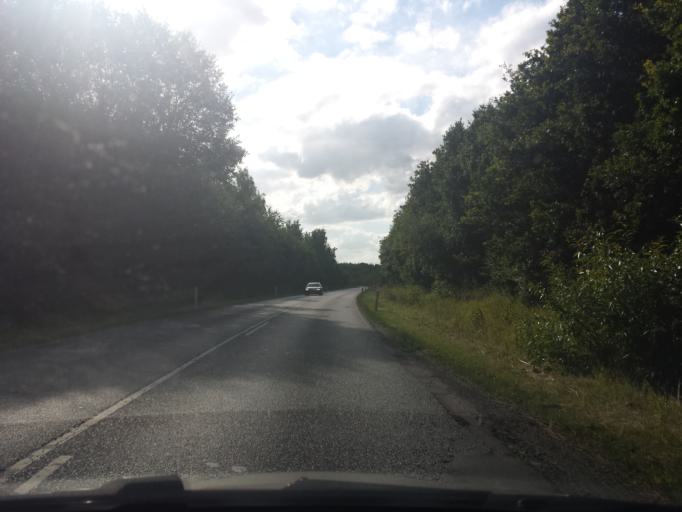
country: DK
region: Capital Region
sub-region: Albertslund Kommune
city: Albertslund
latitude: 55.6824
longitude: 12.3647
